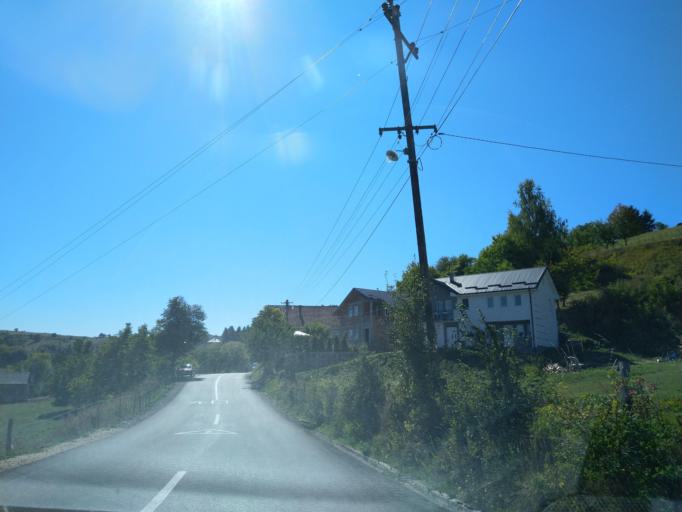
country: RS
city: Sokolovica
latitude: 43.2535
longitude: 20.2290
